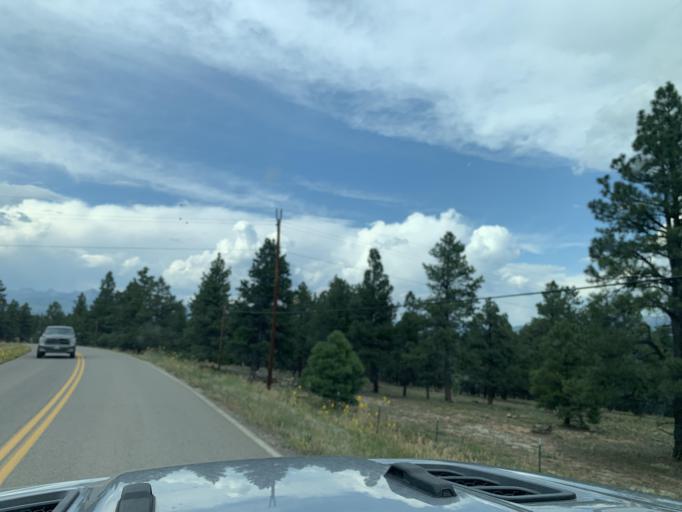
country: US
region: Colorado
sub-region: Archuleta County
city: Pagosa Springs
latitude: 37.2447
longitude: -107.0258
